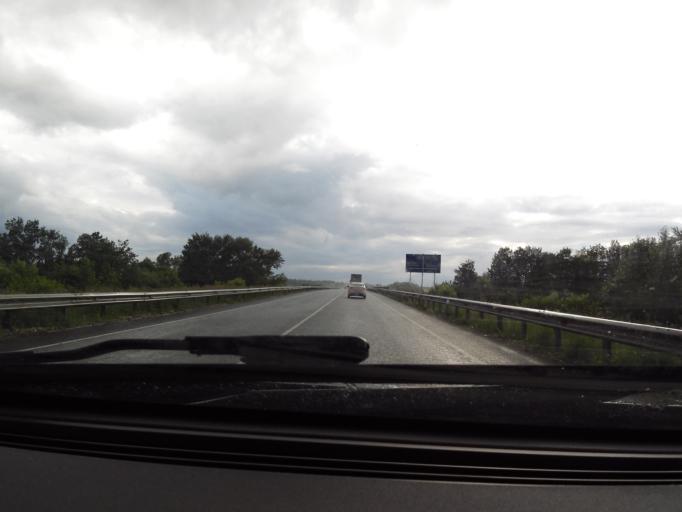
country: RU
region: Tatarstan
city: Nizhniye Vyazovyye
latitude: 55.7248
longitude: 48.4835
